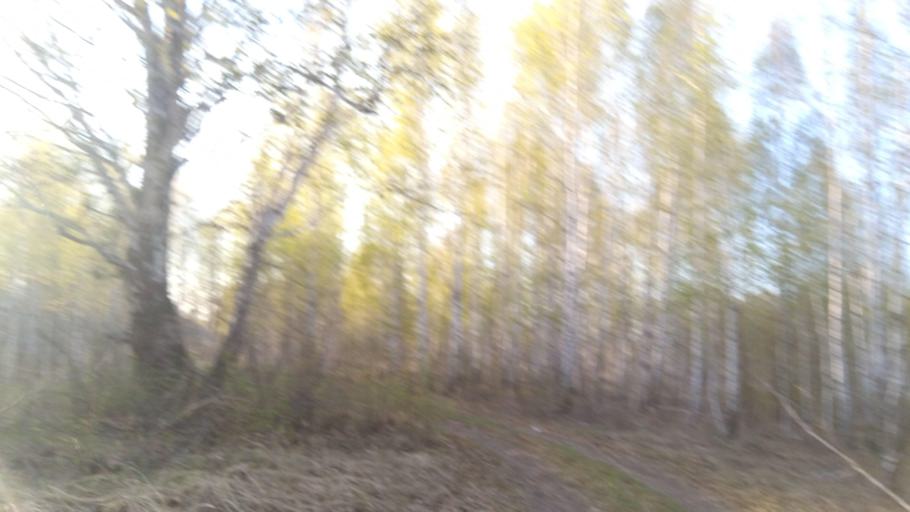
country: RU
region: Chelyabinsk
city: Timiryazevskiy
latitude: 54.9924
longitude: 60.8517
